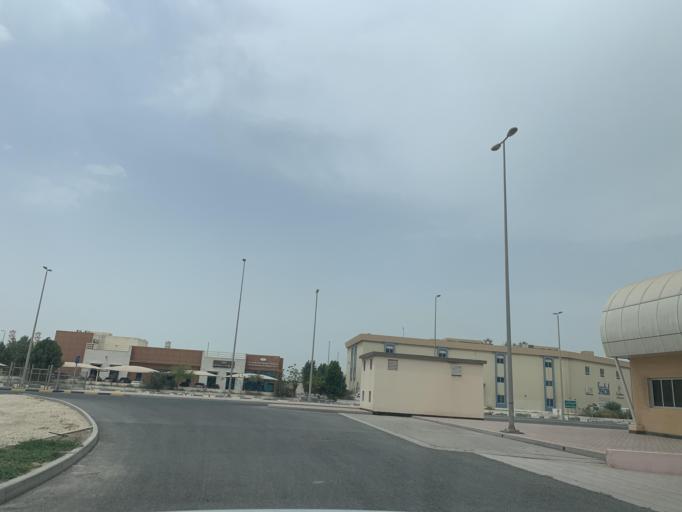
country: BH
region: Muharraq
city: Al Hadd
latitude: 26.2201
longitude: 50.6680
